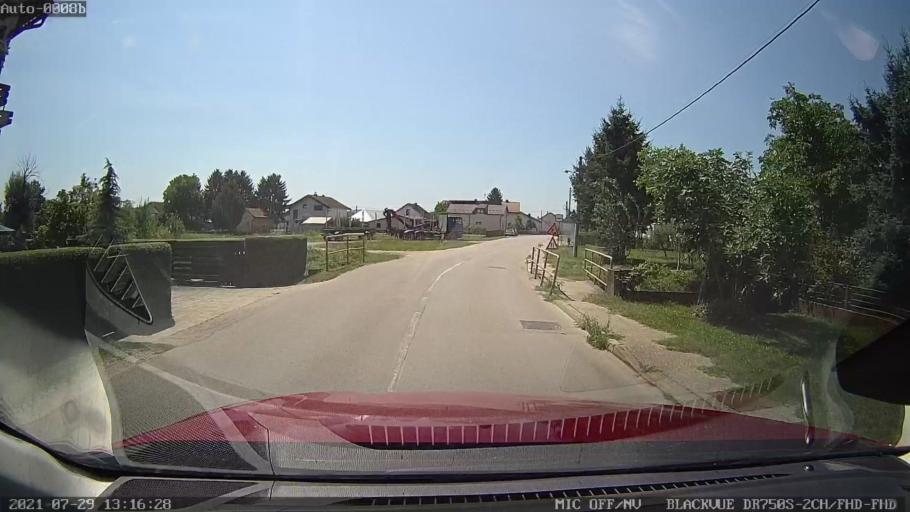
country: HR
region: Medimurska
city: Kursanec
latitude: 46.2790
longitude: 16.3914
